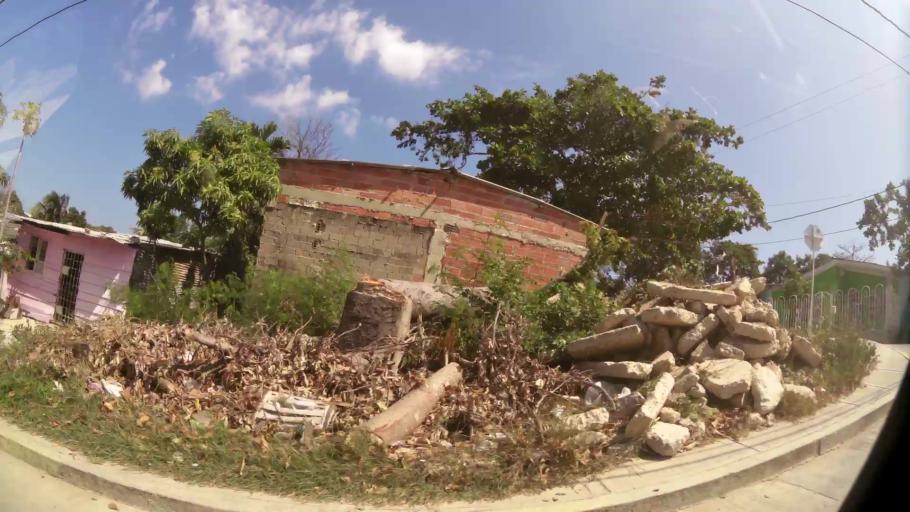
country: CO
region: Atlantico
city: Barranquilla
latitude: 10.9674
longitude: -74.8219
